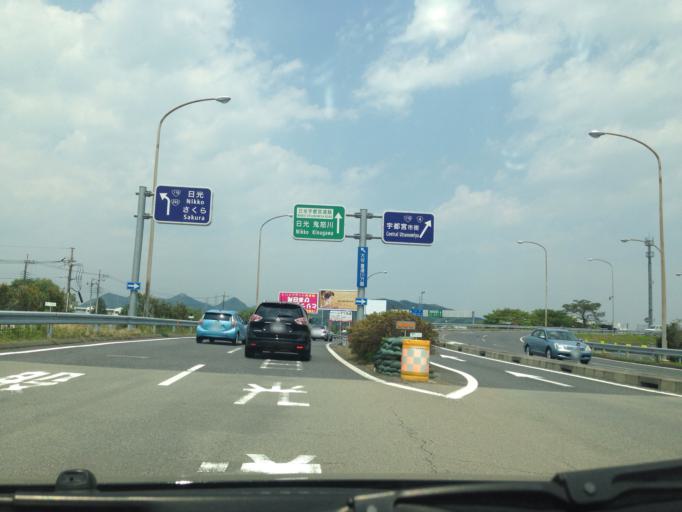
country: JP
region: Tochigi
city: Utsunomiya-shi
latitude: 36.6347
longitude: 139.8449
